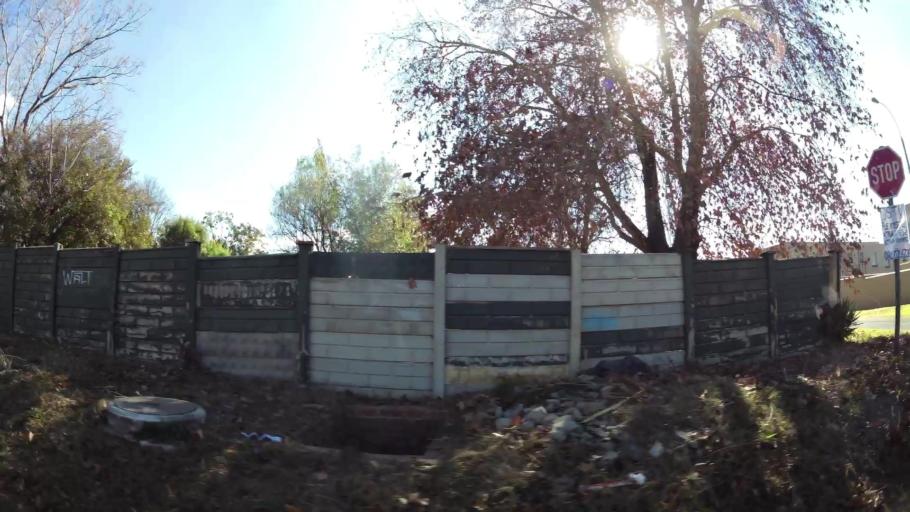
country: ZA
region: Gauteng
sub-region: City of Johannesburg Metropolitan Municipality
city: Roodepoort
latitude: -26.1506
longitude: 27.8366
